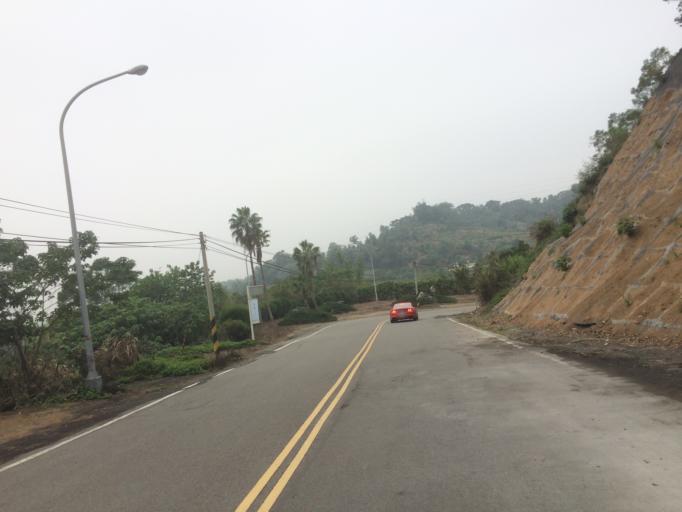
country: TW
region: Taiwan
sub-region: Taichung City
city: Taichung
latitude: 24.1620
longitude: 120.7531
